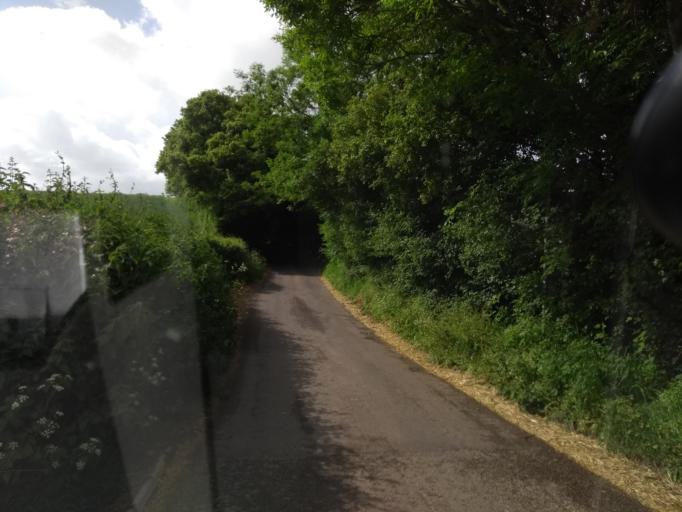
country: GB
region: England
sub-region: Somerset
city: Bishops Lydeard
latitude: 51.1462
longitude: -3.1415
